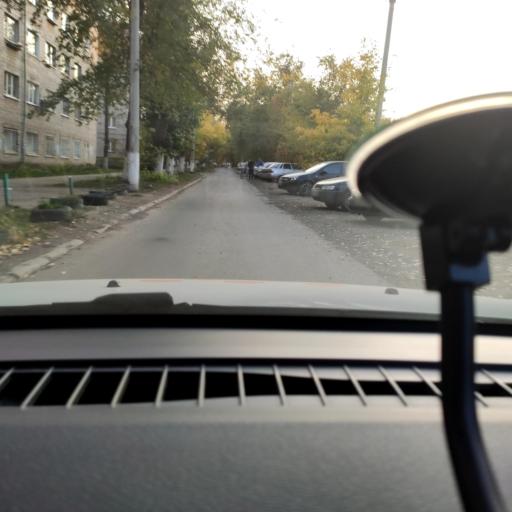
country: RU
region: Samara
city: Samara
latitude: 53.2185
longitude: 50.2326
